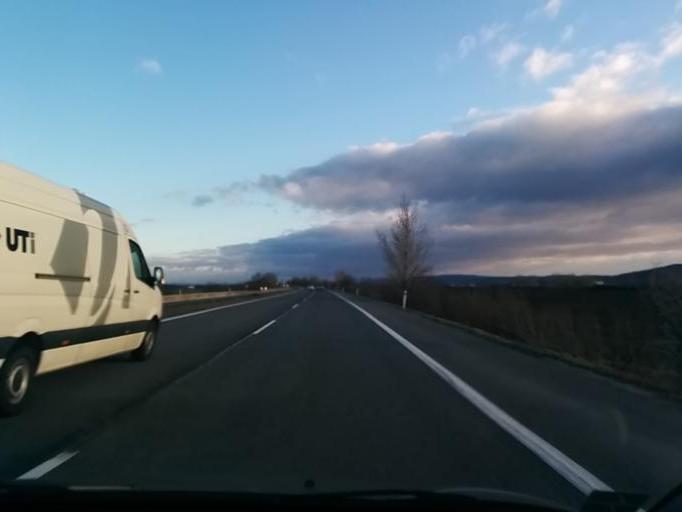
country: SK
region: Trnavsky
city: Leopoldov
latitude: 48.3906
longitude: 17.7428
